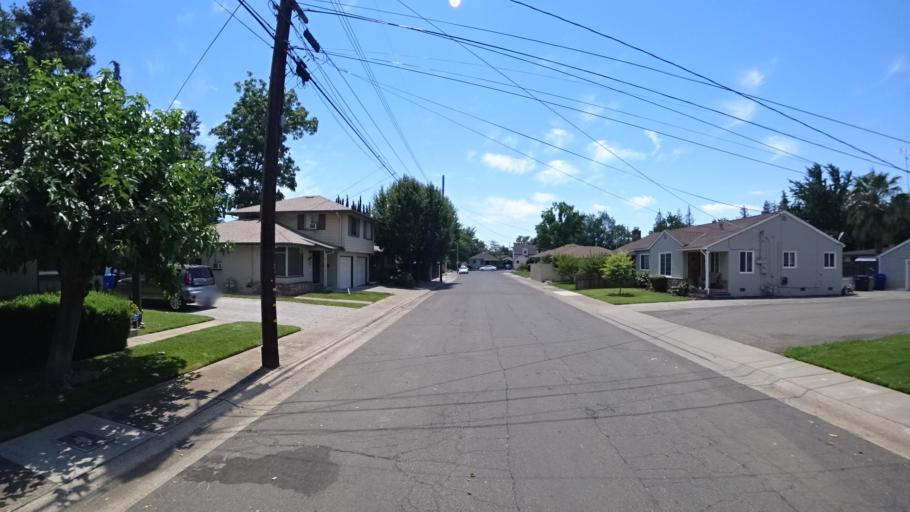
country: US
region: California
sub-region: Sacramento County
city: Sacramento
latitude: 38.5650
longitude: -121.4387
